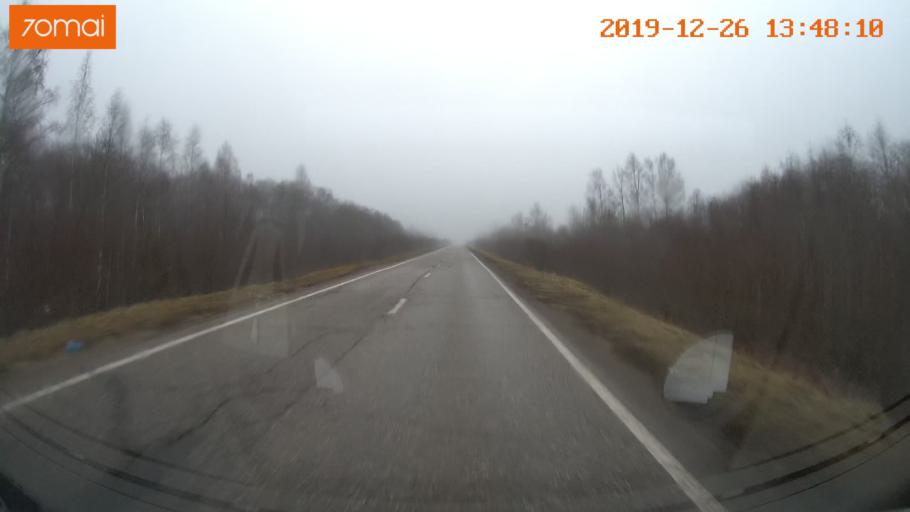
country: RU
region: Vologda
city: Sheksna
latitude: 58.6785
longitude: 38.5441
